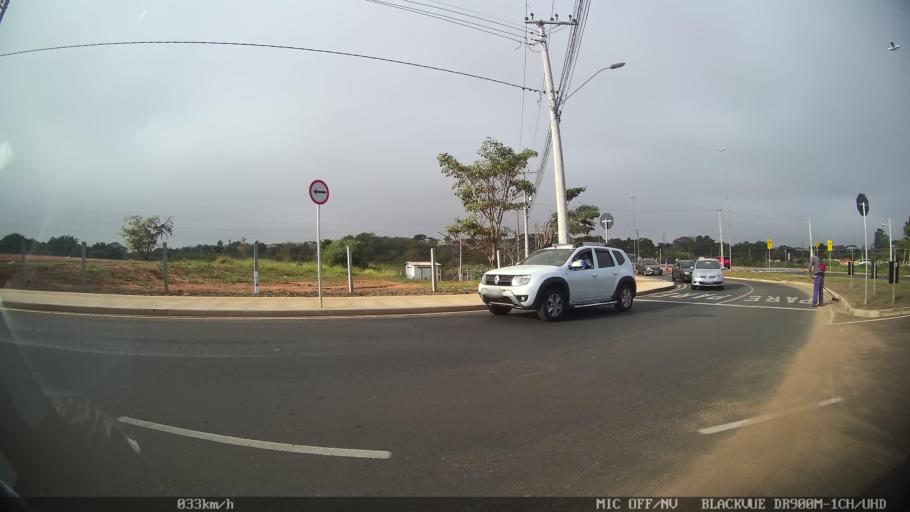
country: BR
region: Sao Paulo
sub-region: Sao Jose Do Rio Preto
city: Sao Jose do Rio Preto
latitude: -20.8252
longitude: -49.3441
